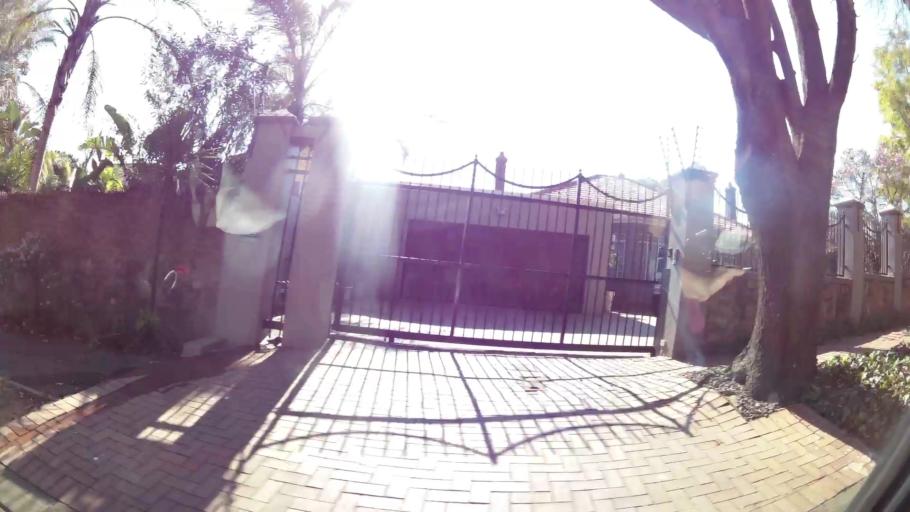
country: ZA
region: Gauteng
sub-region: City of Johannesburg Metropolitan Municipality
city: Johannesburg
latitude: -26.1531
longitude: 28.0297
